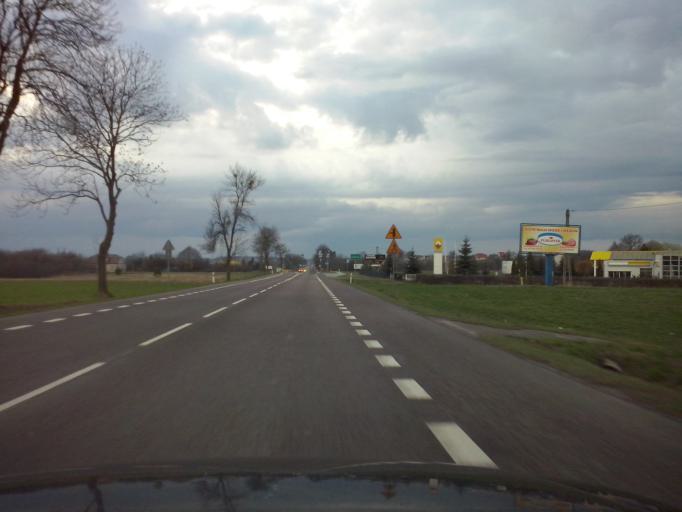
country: PL
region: Lublin Voivodeship
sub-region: Chelm
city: Chelm
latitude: 51.1596
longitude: 23.3972
